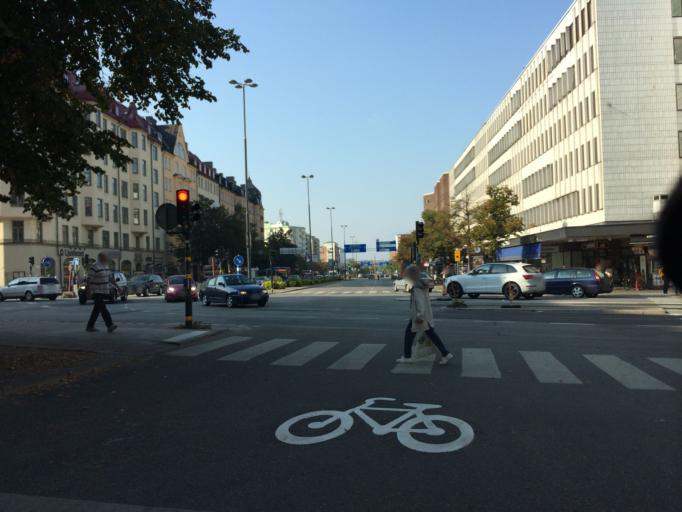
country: SE
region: Stockholm
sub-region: Stockholms Kommun
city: Stockholm
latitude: 59.3323
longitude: 18.0318
